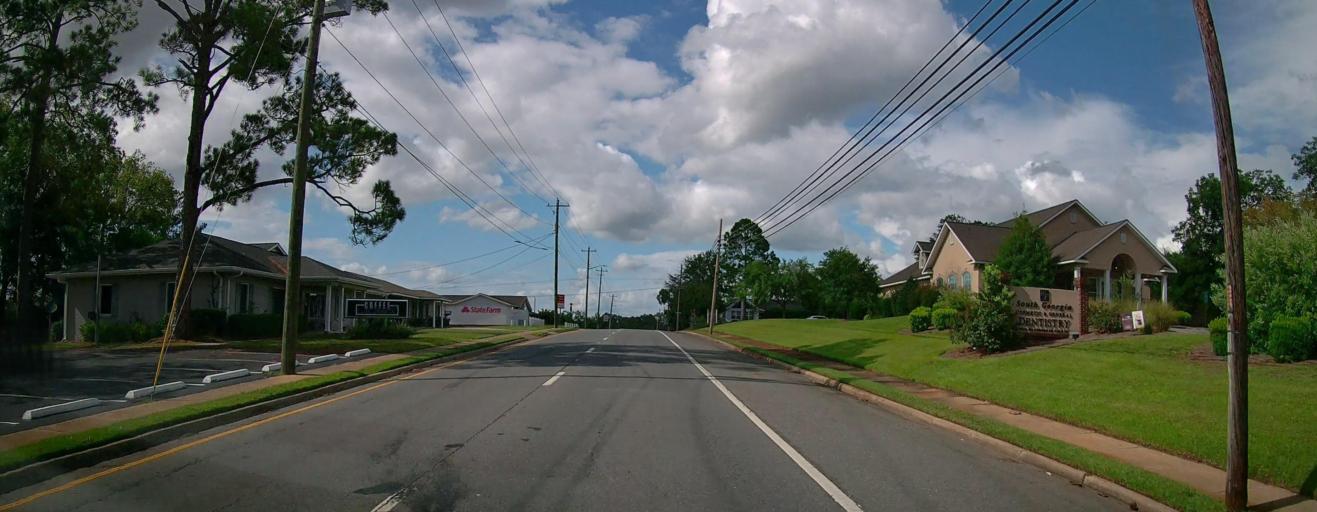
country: US
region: Georgia
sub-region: Coffee County
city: Douglas
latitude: 31.5197
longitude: -82.8493
